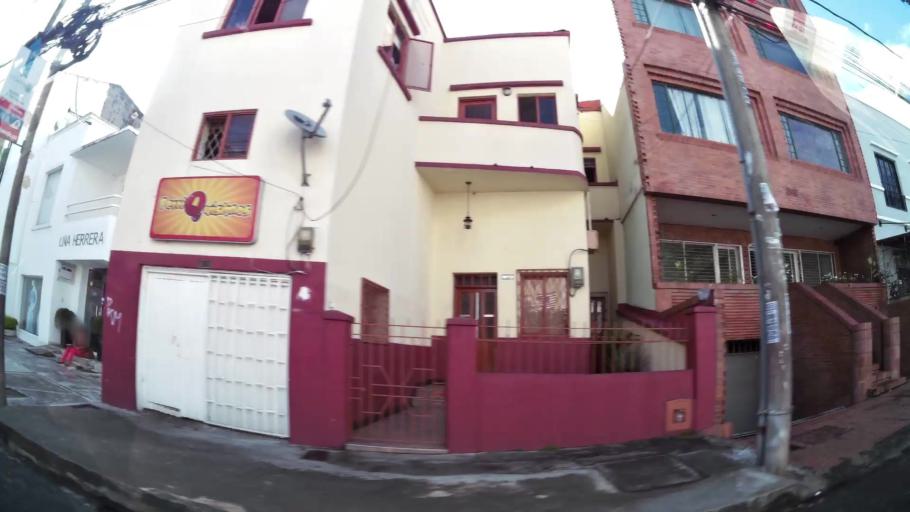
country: CO
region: Valle del Cauca
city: Cali
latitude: 3.4606
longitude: -76.5332
